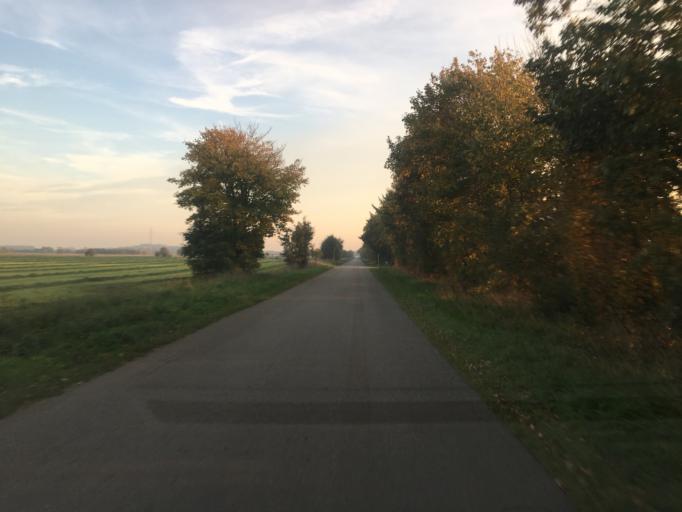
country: DK
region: South Denmark
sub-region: Tonder Kommune
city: Toftlund
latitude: 55.0462
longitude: 9.1102
